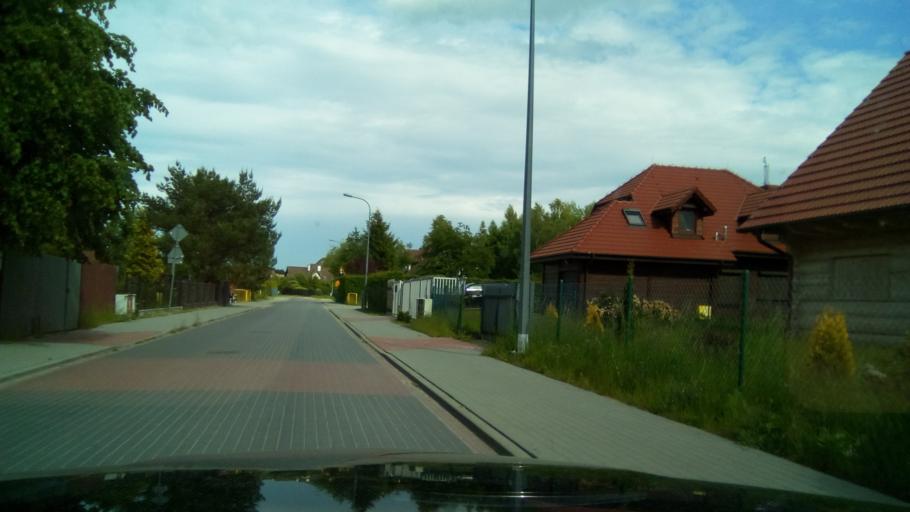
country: PL
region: Pomeranian Voivodeship
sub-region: Powiat pucki
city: Wierzchucino
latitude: 54.8255
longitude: 18.0804
